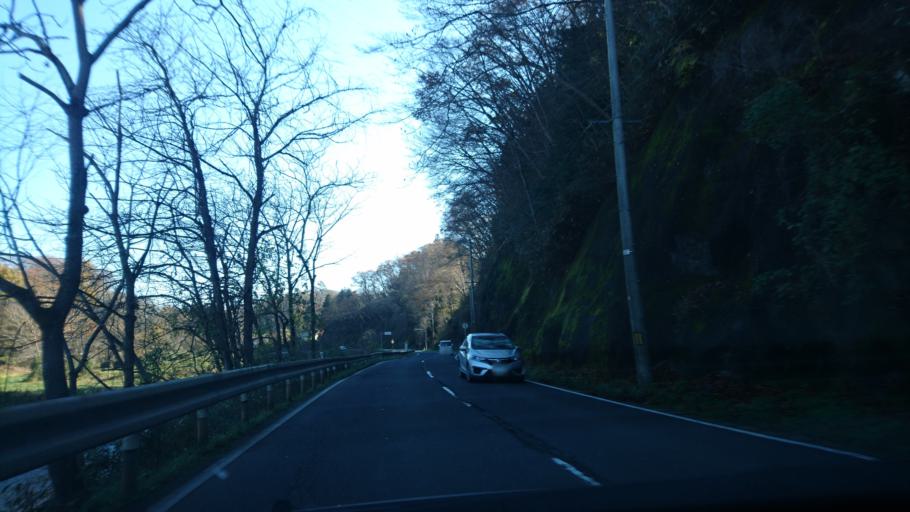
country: JP
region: Iwate
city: Ichinoseki
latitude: 38.9922
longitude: 141.2959
